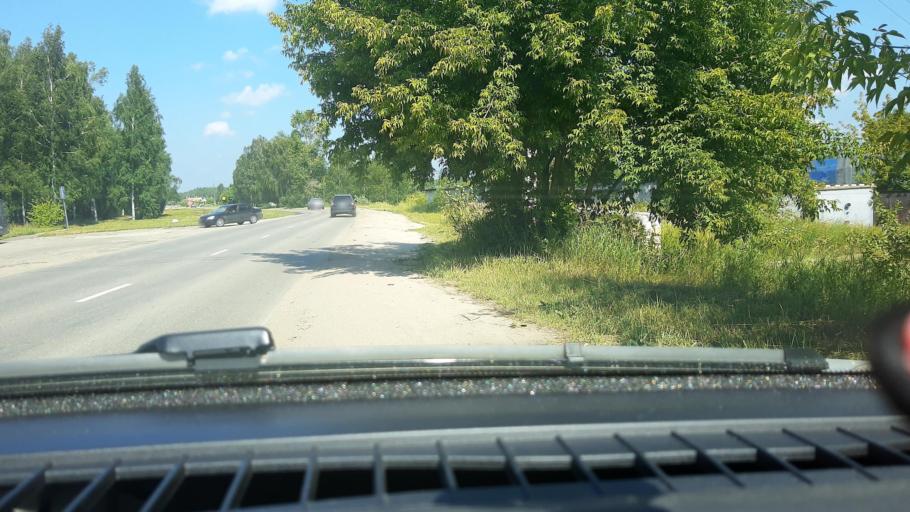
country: RU
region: Nizjnij Novgorod
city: Afonino
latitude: 56.2995
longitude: 44.1898
